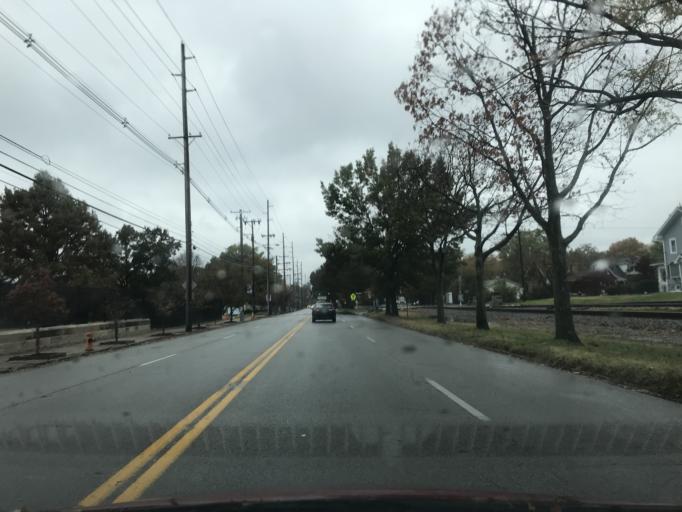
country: US
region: Kentucky
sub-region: Jefferson County
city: Saint Matthews
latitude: 38.2546
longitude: -85.6823
